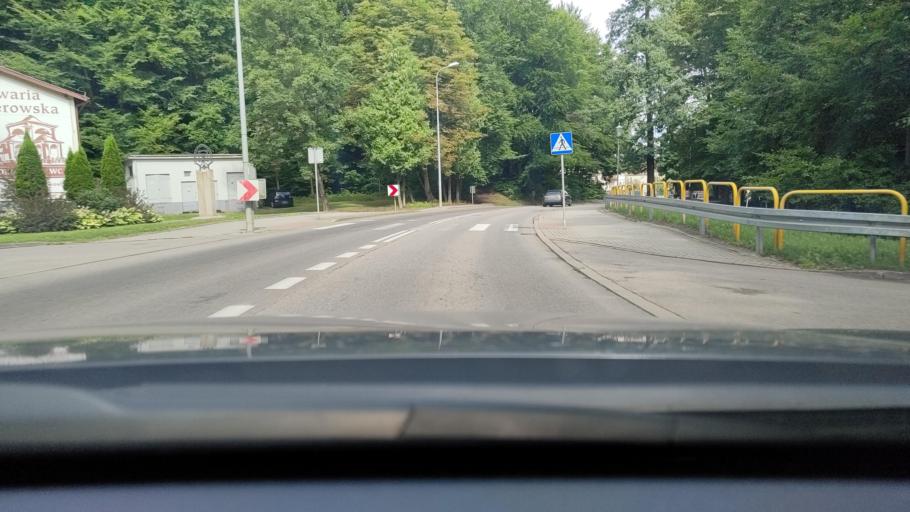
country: PL
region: Pomeranian Voivodeship
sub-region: Powiat wejherowski
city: Wejherowo
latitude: 54.5953
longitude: 18.2332
